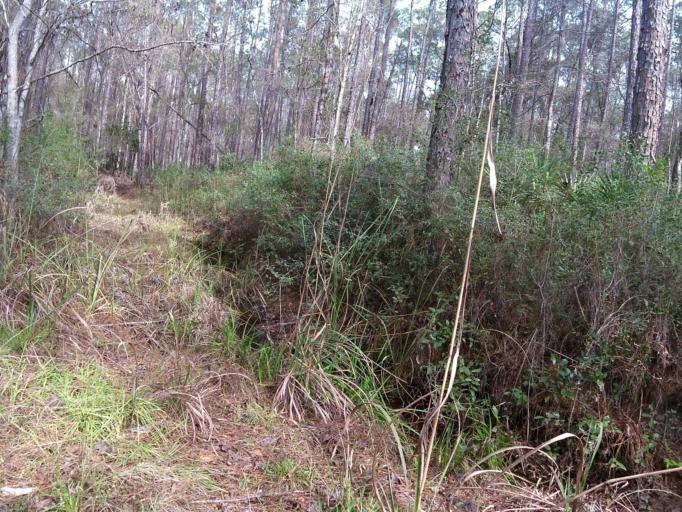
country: US
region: Florida
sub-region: Clay County
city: Middleburg
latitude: 30.1259
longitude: -81.9081
